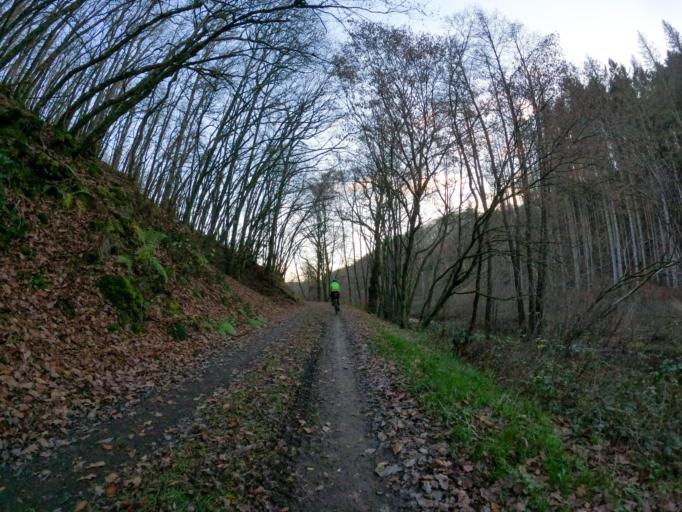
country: LU
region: Diekirch
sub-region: Canton de Wiltz
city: Bavigne
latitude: 49.9343
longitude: 5.8424
